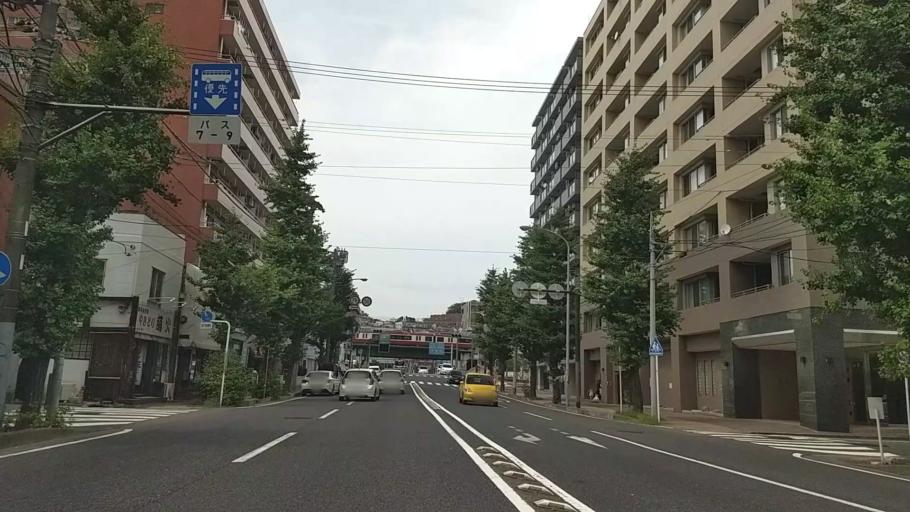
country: JP
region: Kanagawa
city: Yokohama
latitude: 35.4367
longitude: 139.6179
